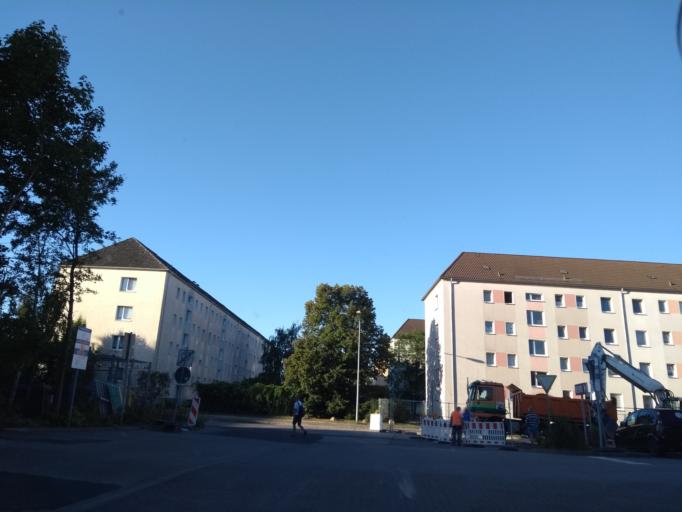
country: DE
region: Brandenburg
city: Lubbenau
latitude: 51.8599
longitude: 13.9533
